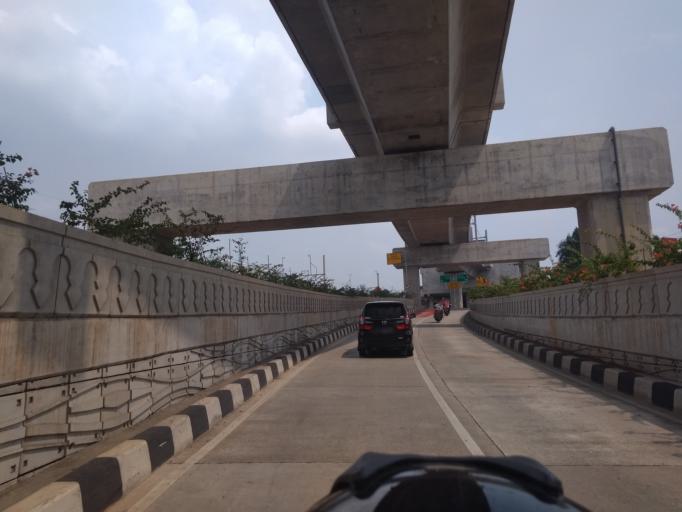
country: ID
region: Banten
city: South Tangerang
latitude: -6.2893
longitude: 106.7752
